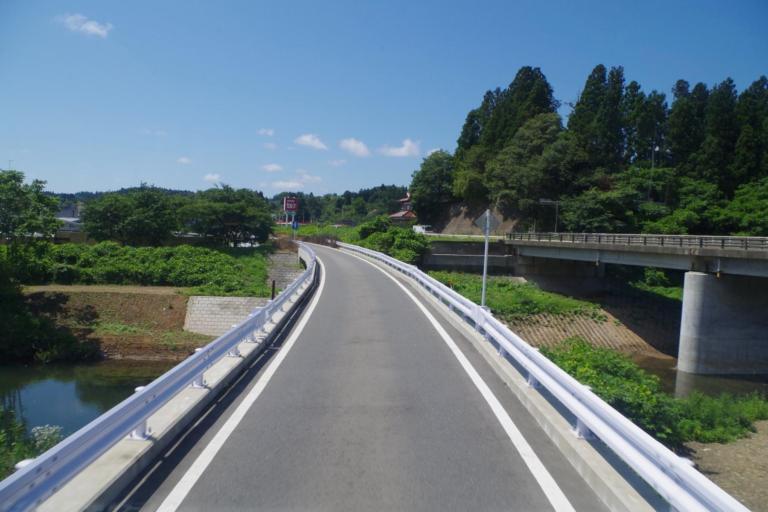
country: JP
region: Iwate
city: Ofunato
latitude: 38.9104
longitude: 141.5480
